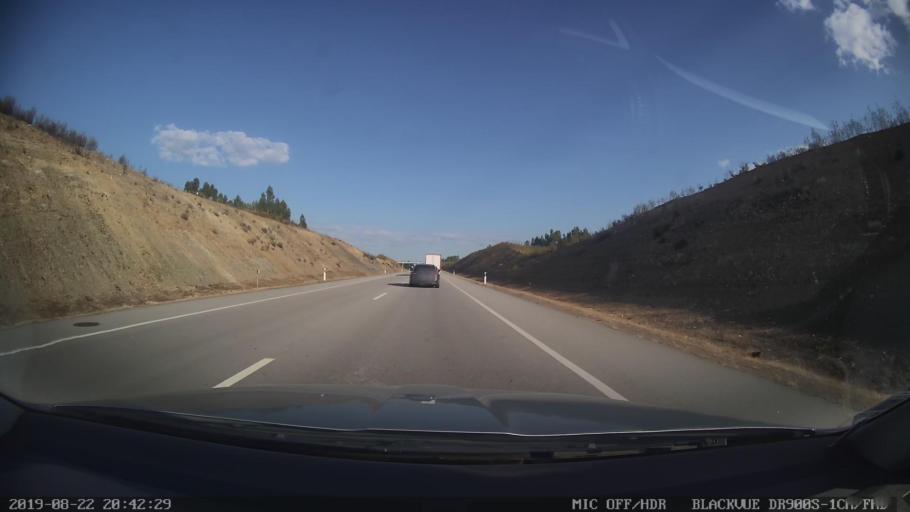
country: PT
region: Castelo Branco
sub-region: Proenca-A-Nova
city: Proenca-a-Nova
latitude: 39.6948
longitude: -7.8172
